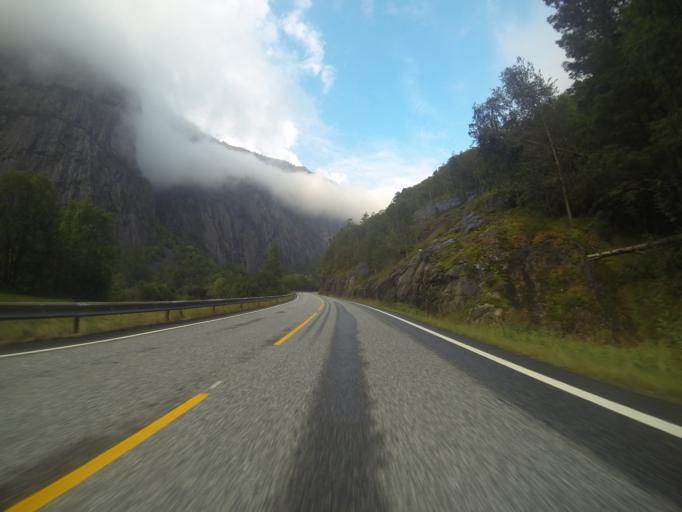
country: NO
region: Rogaland
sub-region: Sauda
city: Sauda
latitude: 59.8744
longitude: 6.3918
